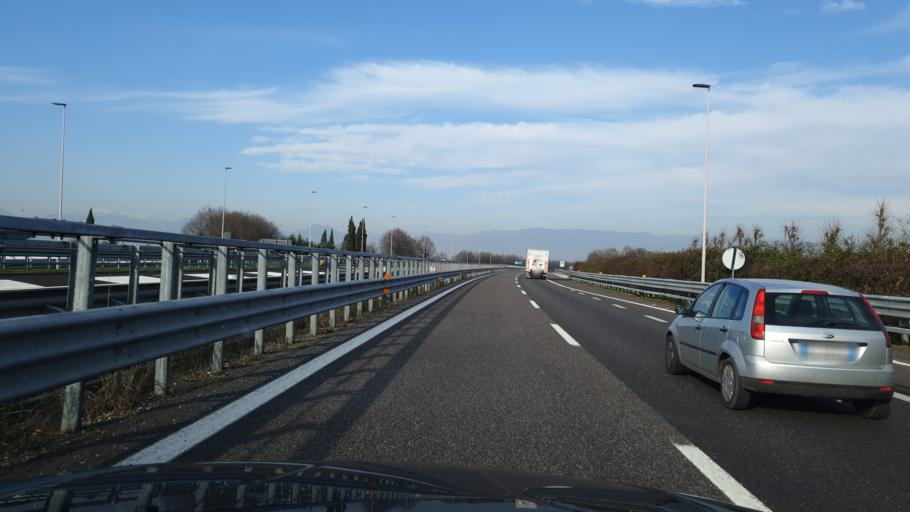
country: IT
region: Veneto
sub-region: Provincia di Vicenza
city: Lisiera
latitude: 45.5797
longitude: 11.6010
